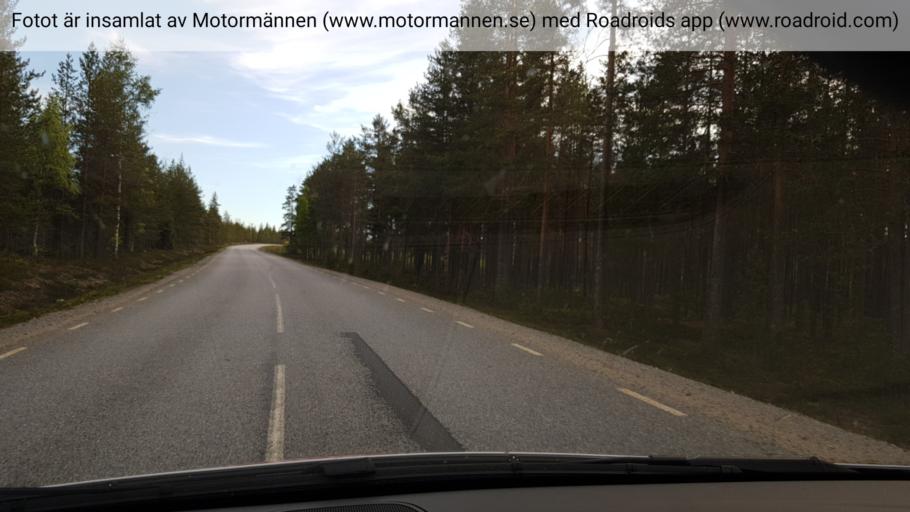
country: SE
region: Vaesterbotten
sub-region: Umea Kommun
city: Saevar
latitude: 63.9669
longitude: 20.5072
